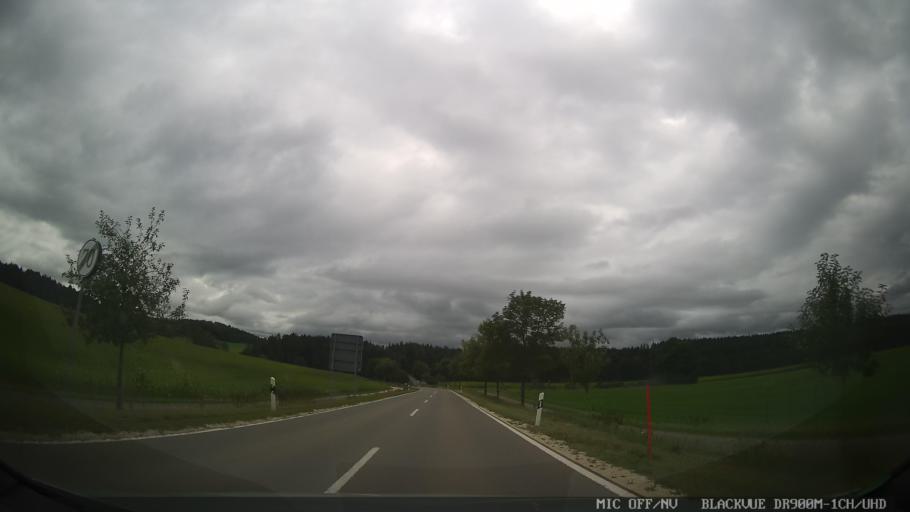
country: DE
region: Baden-Wuerttemberg
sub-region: Freiburg Region
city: Neuhausen ob Eck
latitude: 47.9629
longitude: 8.9304
